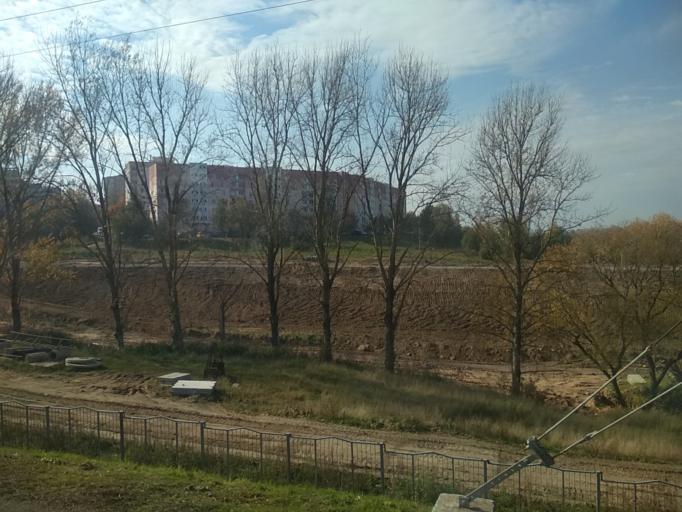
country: BY
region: Minsk
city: Syenitsa
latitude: 53.8551
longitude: 27.5576
